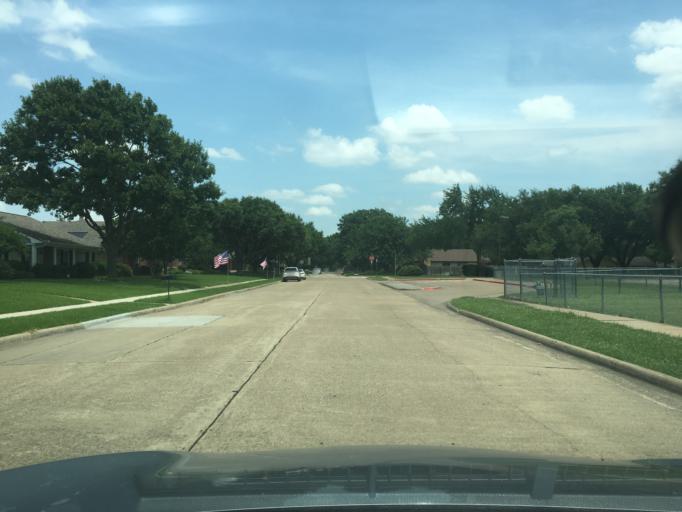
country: US
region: Texas
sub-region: Dallas County
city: Richardson
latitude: 32.9549
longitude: -96.6898
